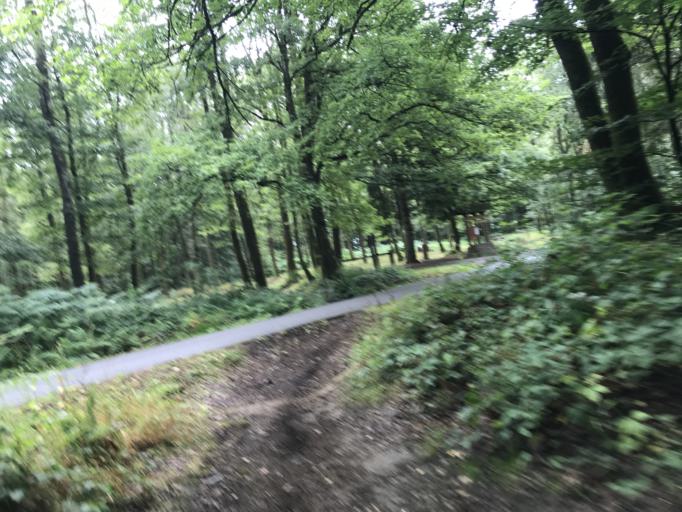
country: FR
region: Champagne-Ardenne
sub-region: Departement des Ardennes
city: Thilay
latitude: 49.8929
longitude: 4.7830
